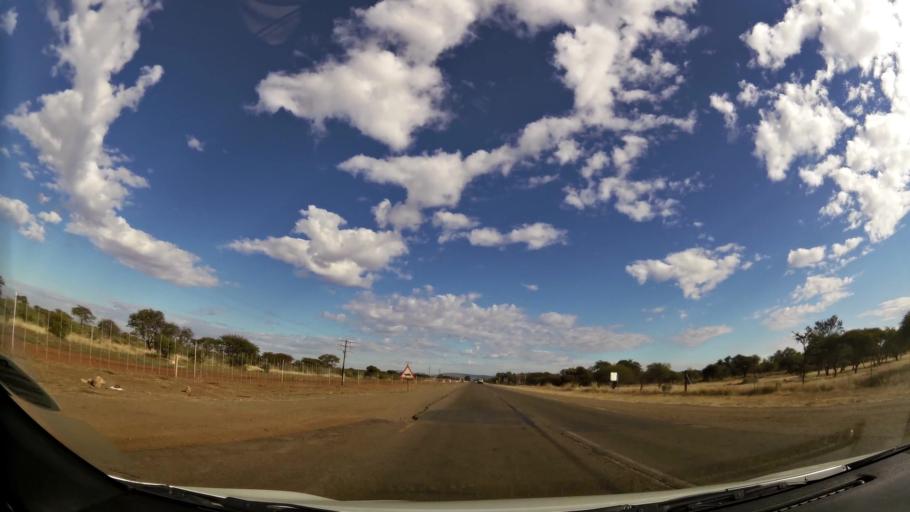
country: ZA
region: Limpopo
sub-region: Waterberg District Municipality
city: Bela-Bela
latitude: -24.9164
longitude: 28.3666
